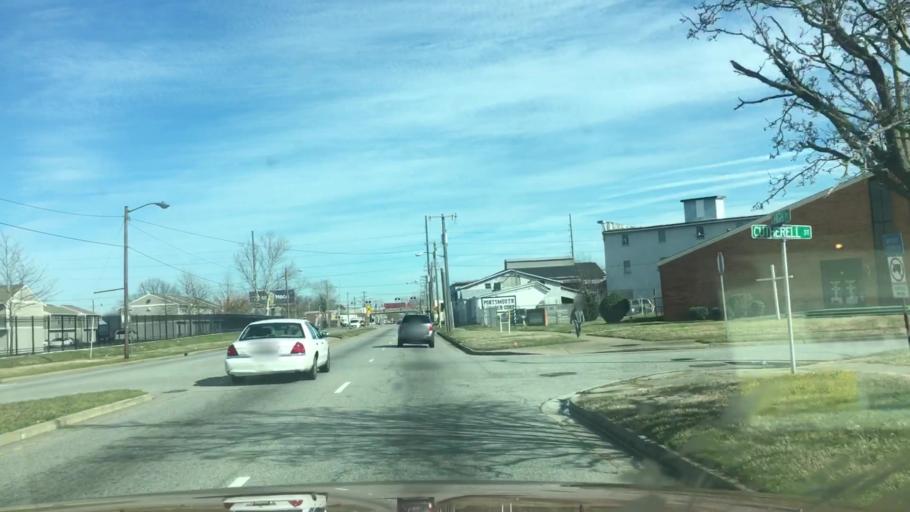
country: US
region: Virginia
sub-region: City of Portsmouth
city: Portsmouth
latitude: 36.8346
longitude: -76.3328
